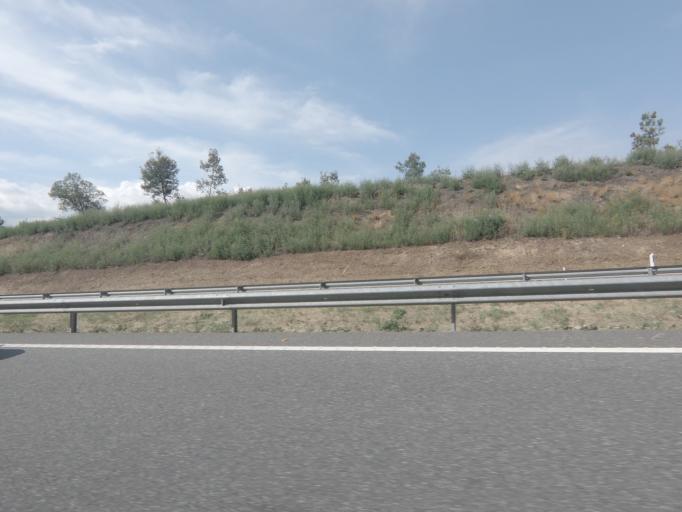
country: ES
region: Galicia
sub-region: Provincia de Ourense
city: Toen
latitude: 42.3332
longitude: -7.9662
